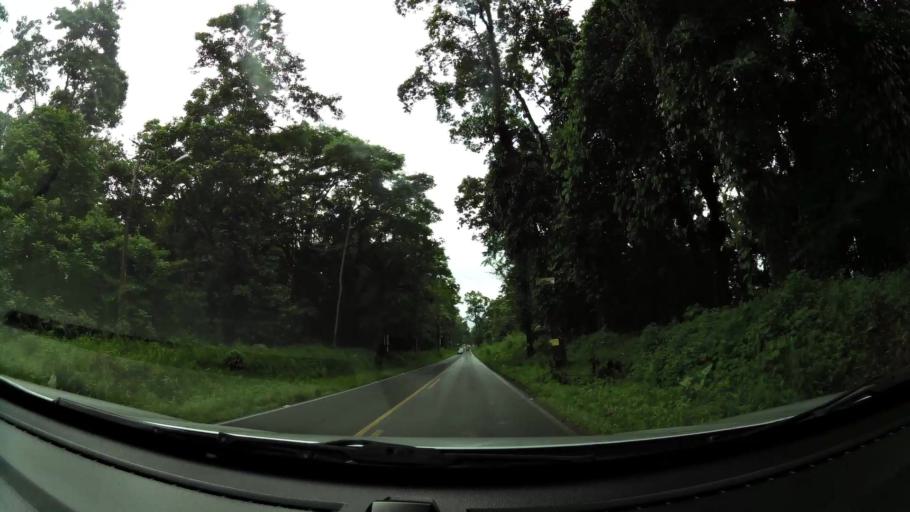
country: CR
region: Limon
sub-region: Canton de Pococi
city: Guapiles
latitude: 10.2094
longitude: -83.7895
